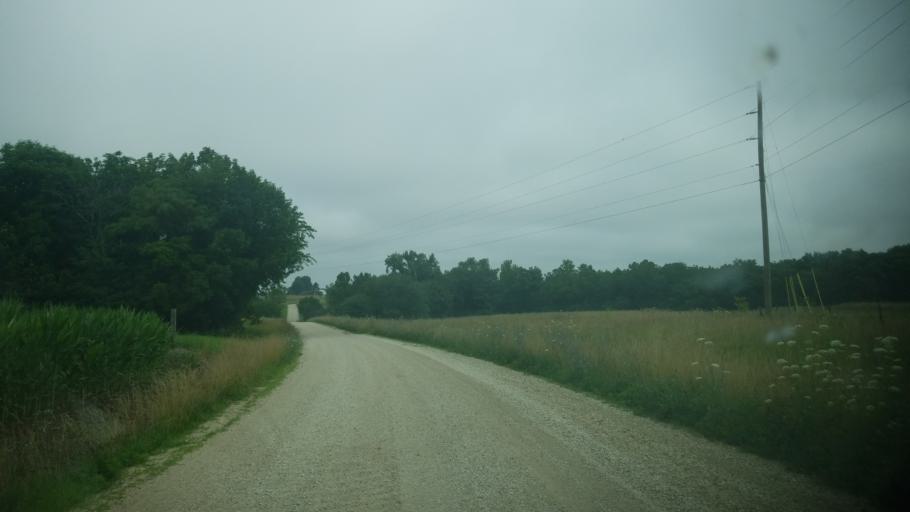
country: US
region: Missouri
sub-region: Pike County
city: Bowling Green
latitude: 39.3551
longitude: -91.2617
